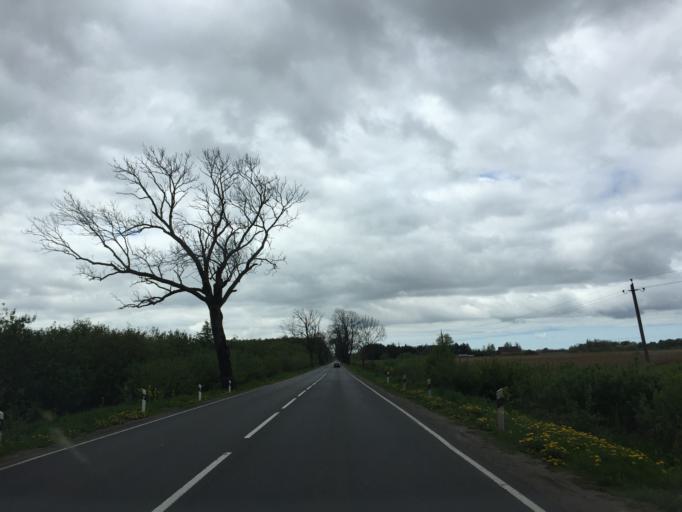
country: RU
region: Kaliningrad
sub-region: Gorod Kaliningrad
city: Kaliningrad
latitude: 54.6584
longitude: 20.3951
